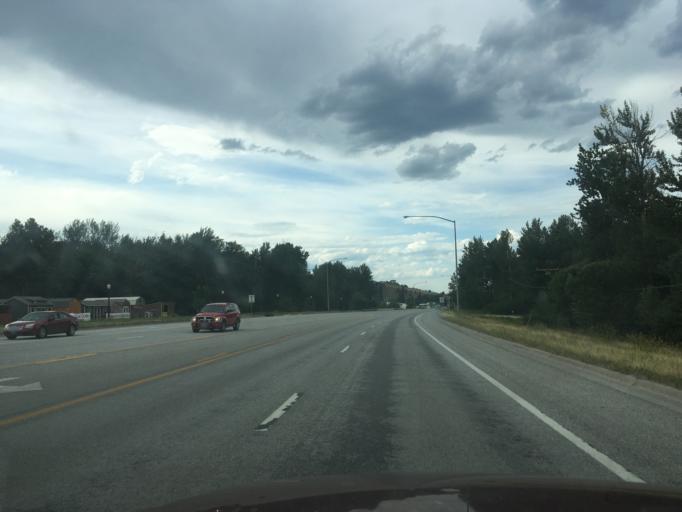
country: US
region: Montana
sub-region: Missoula County
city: Lolo
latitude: 46.7476
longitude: -114.0826
